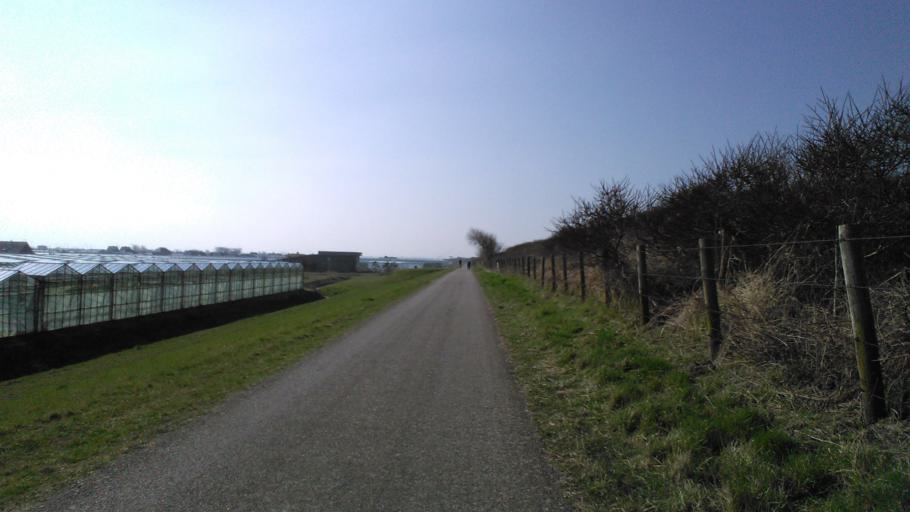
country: NL
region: South Holland
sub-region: Gemeente Westland
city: Monster
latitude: 52.0229
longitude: 4.1584
